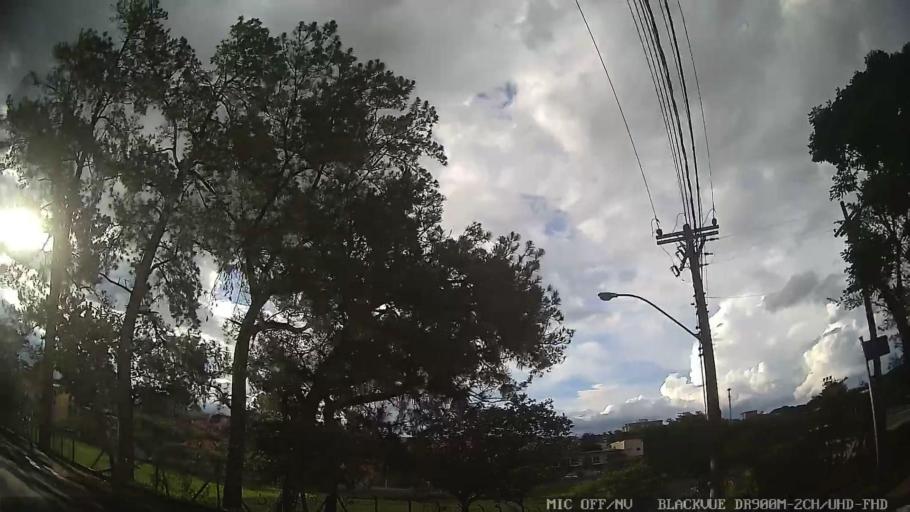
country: BR
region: Sao Paulo
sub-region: Jaguariuna
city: Jaguariuna
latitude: -22.7007
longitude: -46.9874
